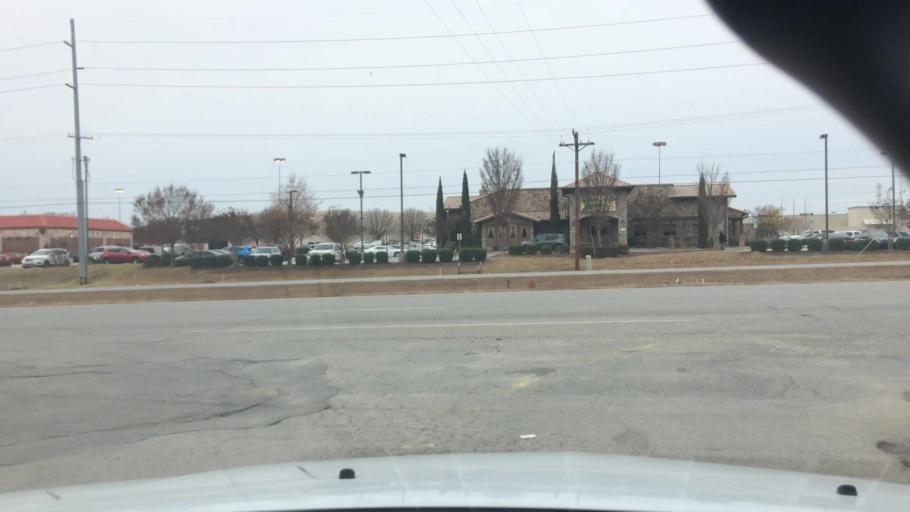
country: US
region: North Carolina
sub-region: Nash County
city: Rocky Mount
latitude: 35.9727
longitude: -77.8036
